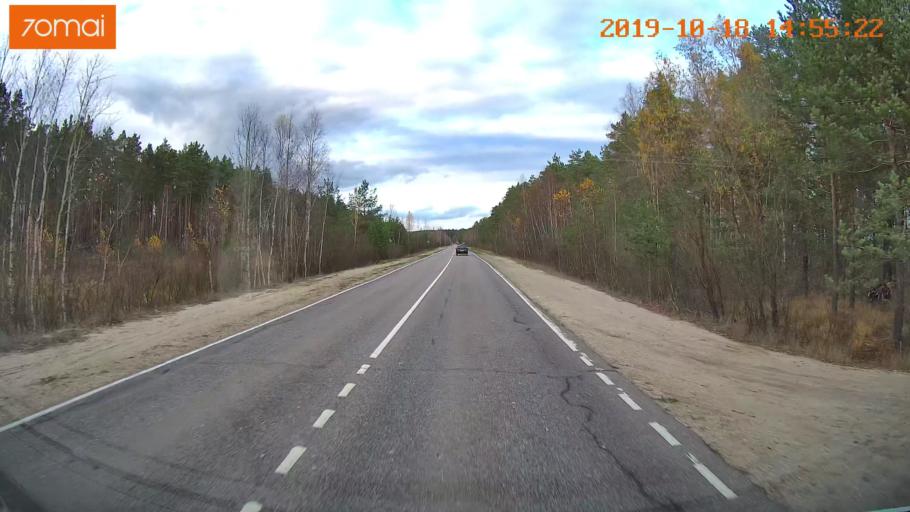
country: RU
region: Vladimir
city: Kurlovo
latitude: 55.4512
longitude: 40.5886
